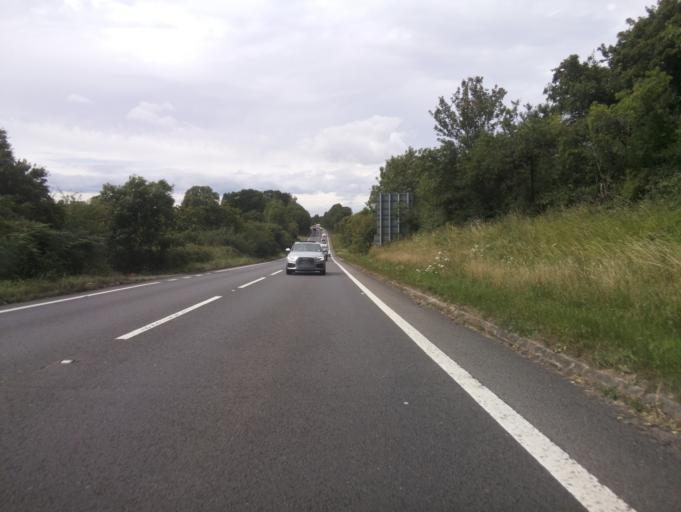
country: GB
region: England
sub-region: Somerset
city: Yeovil
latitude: 50.8874
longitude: -2.6097
